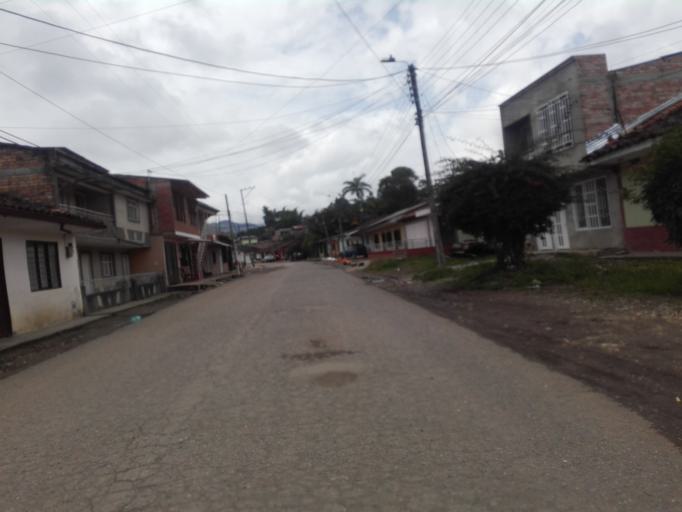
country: CO
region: Cauca
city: Popayan
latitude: 2.3510
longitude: -76.6767
